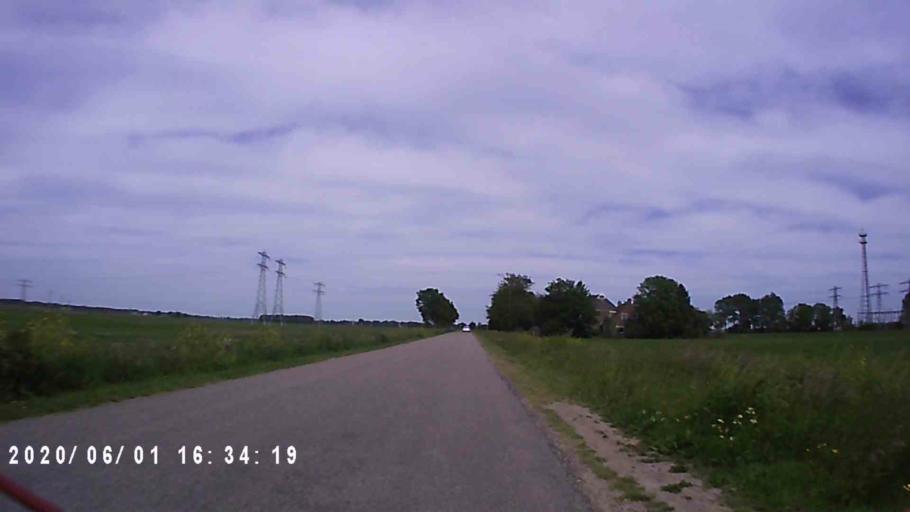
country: NL
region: Friesland
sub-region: Gemeente Leeuwarden
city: Camminghaburen
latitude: 53.1925
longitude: 5.8715
